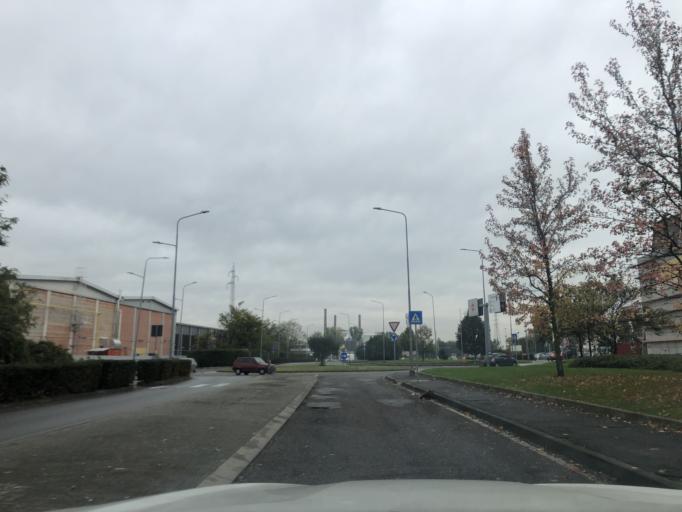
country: IT
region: Lombardy
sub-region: Citta metropolitana di Milano
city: Cesano Boscone
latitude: 45.4353
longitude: 9.0885
